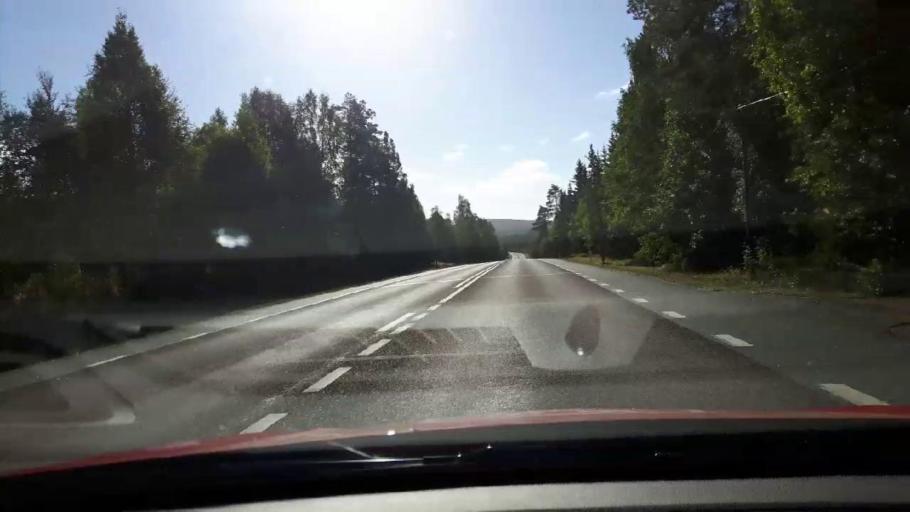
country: SE
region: Jaemtland
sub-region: Braecke Kommun
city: Braecke
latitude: 62.8246
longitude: 15.3238
